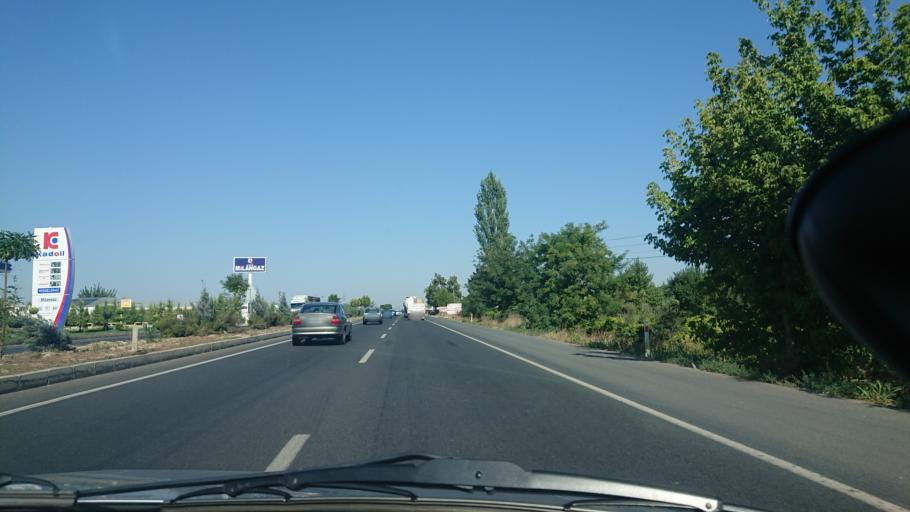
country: TR
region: Manisa
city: Ahmetli
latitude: 38.5018
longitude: 27.8736
